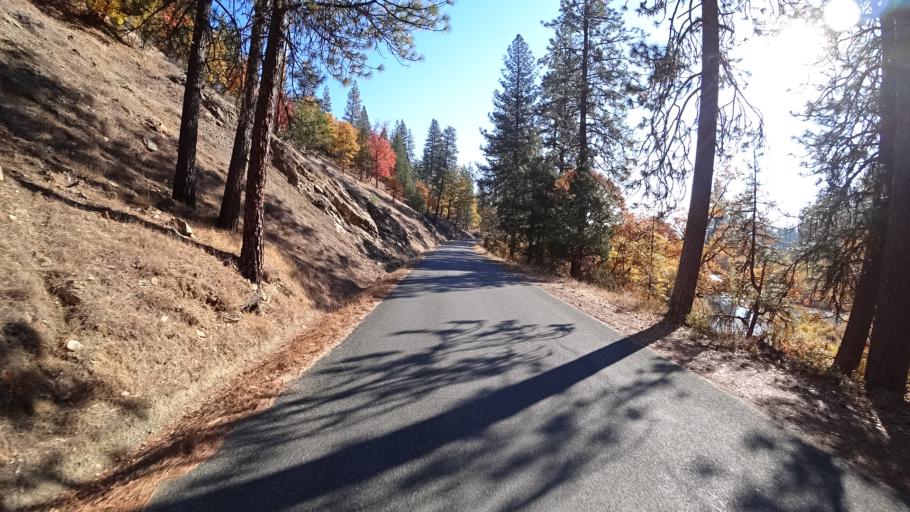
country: US
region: California
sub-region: Siskiyou County
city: Yreka
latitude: 41.6417
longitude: -122.9995
